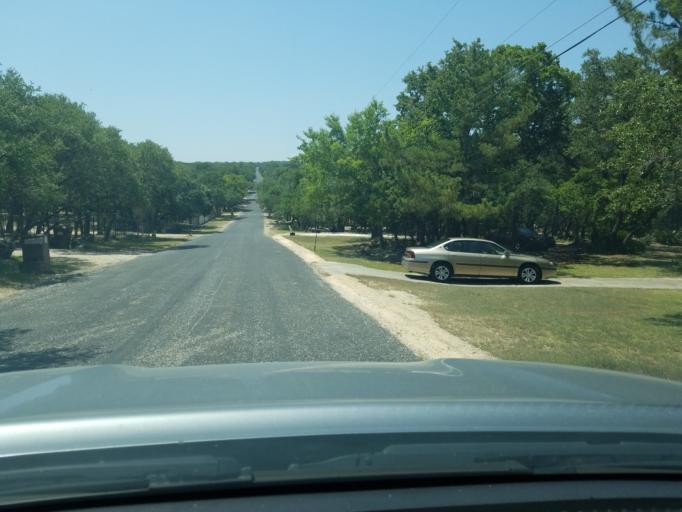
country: US
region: Texas
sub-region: Bexar County
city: Timberwood Park
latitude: 29.7208
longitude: -98.4924
